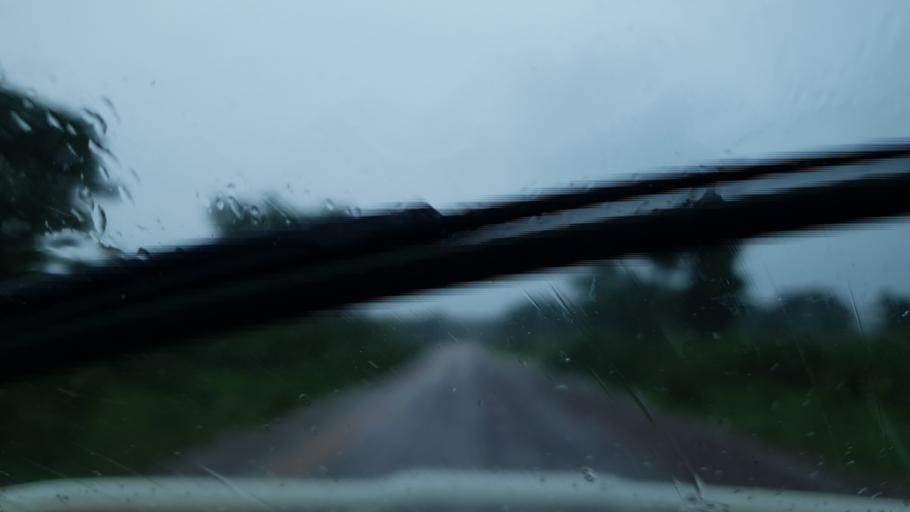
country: ML
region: Sikasso
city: Kolondieba
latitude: 11.6146
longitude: -6.6768
